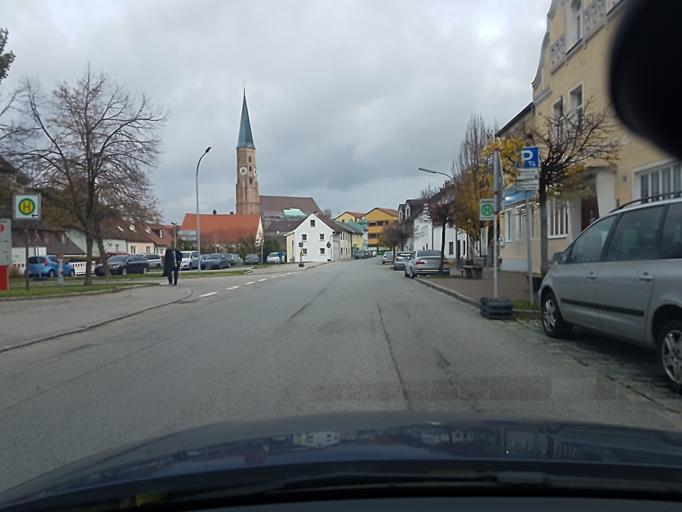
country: DE
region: Bavaria
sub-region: Lower Bavaria
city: Dingolfing
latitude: 48.6264
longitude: 12.4965
